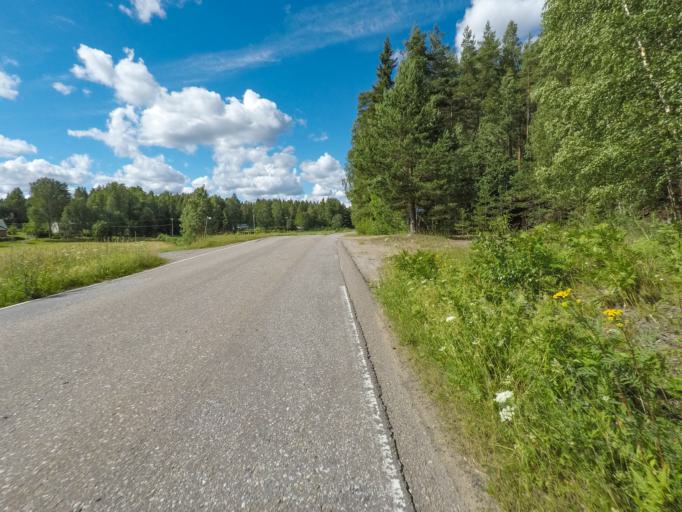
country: FI
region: South Karelia
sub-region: Lappeenranta
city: Joutseno
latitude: 61.1097
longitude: 28.3696
